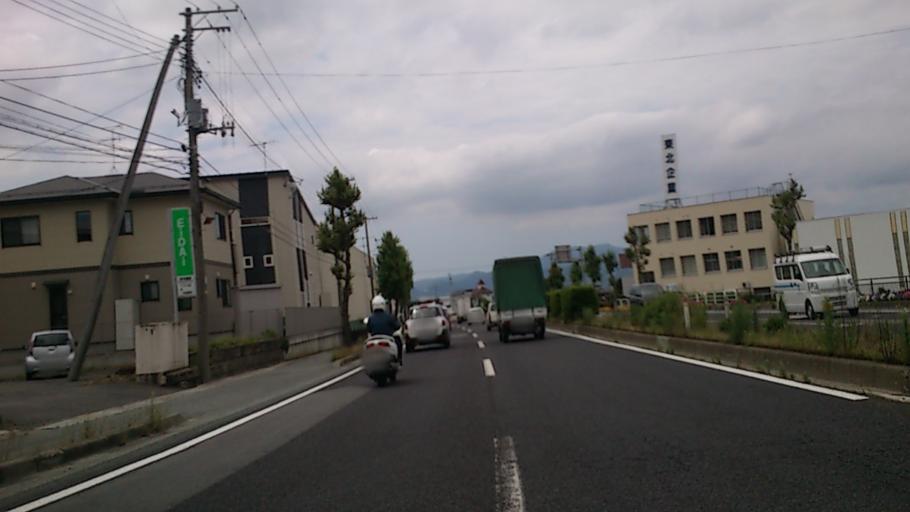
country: JP
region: Yamagata
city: Yamagata-shi
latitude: 38.2293
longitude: 140.3394
